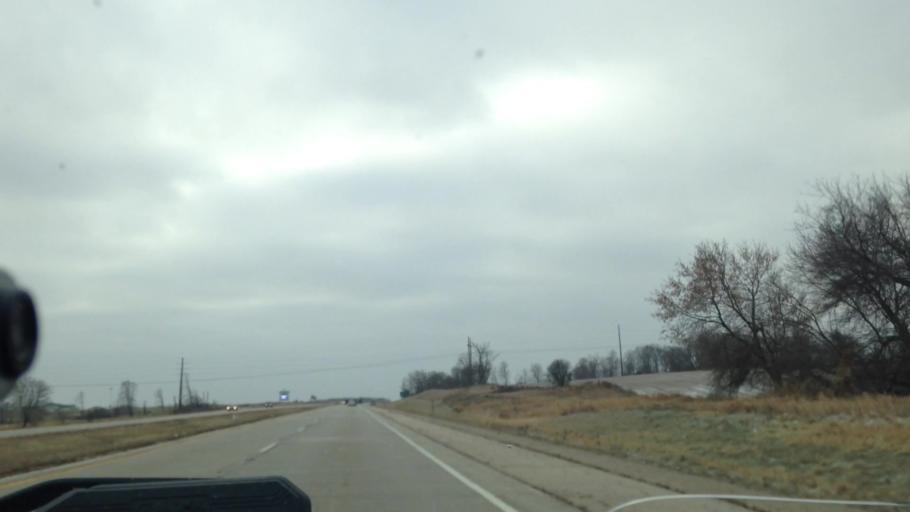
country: US
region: Wisconsin
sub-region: Washington County
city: Jackson
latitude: 43.3644
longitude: -88.1928
